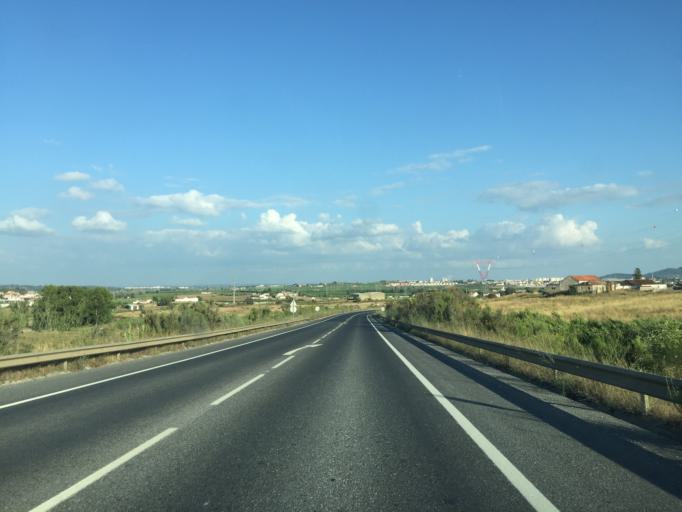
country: PT
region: Lisbon
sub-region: Alenquer
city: Alenquer
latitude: 39.0640
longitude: -8.9980
